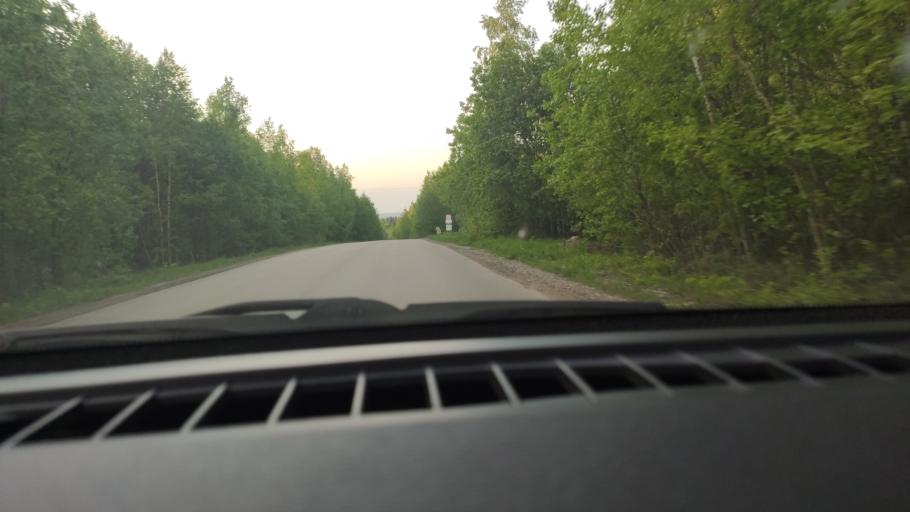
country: RU
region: Perm
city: Kondratovo
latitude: 58.0645
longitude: 56.0023
